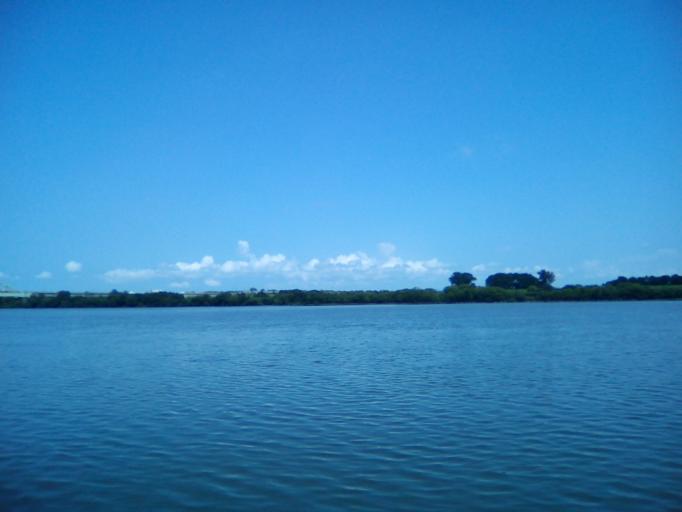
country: JP
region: Hokkaido
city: Ebetsu
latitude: 43.1329
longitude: 141.5168
